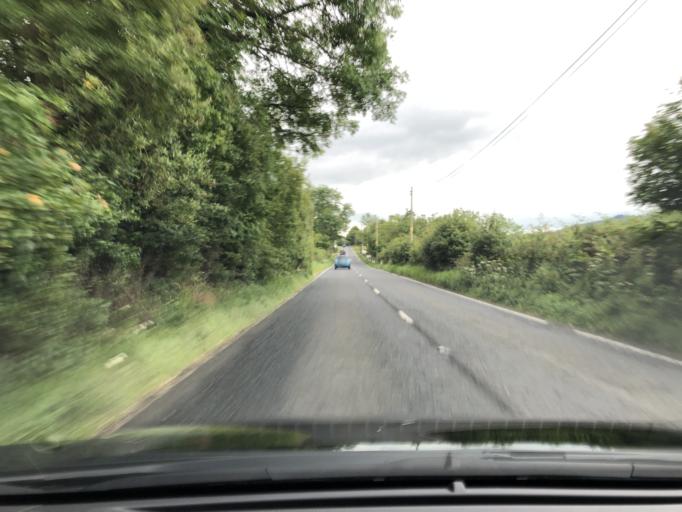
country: GB
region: Northern Ireland
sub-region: Down District
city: Castlewellan
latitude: 54.2686
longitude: -5.9060
